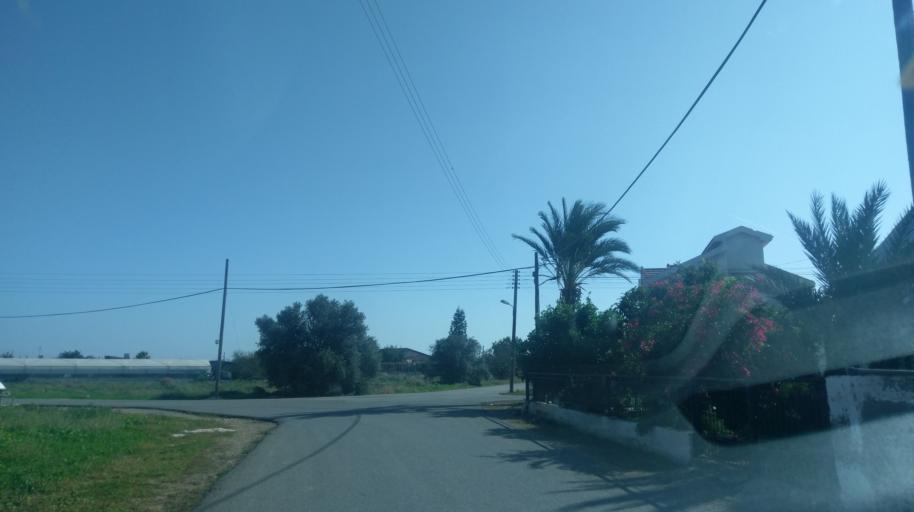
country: CY
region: Ammochostos
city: Trikomo
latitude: 35.2366
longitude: 33.8583
